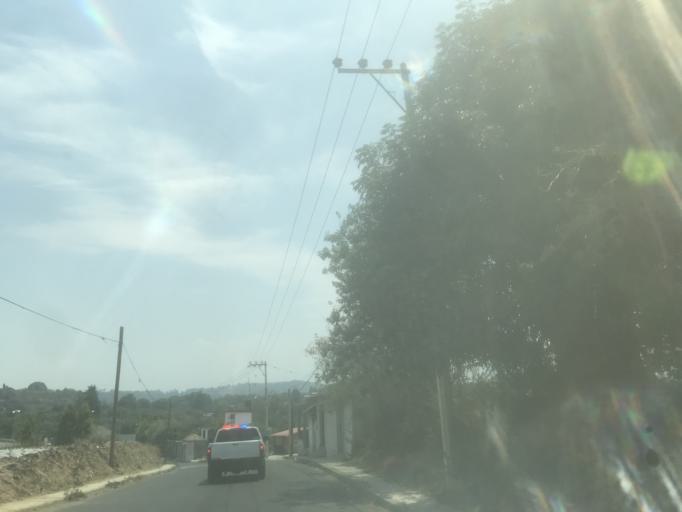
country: MX
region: Mexico
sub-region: Ozumba
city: San Jose Tlacotitlan
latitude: 18.9884
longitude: -98.8055
